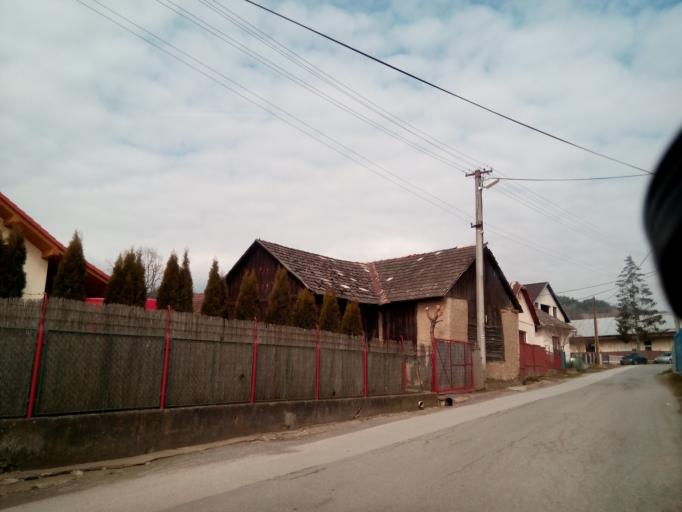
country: SK
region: Presovsky
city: Sabinov
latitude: 49.0473
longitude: 21.0166
